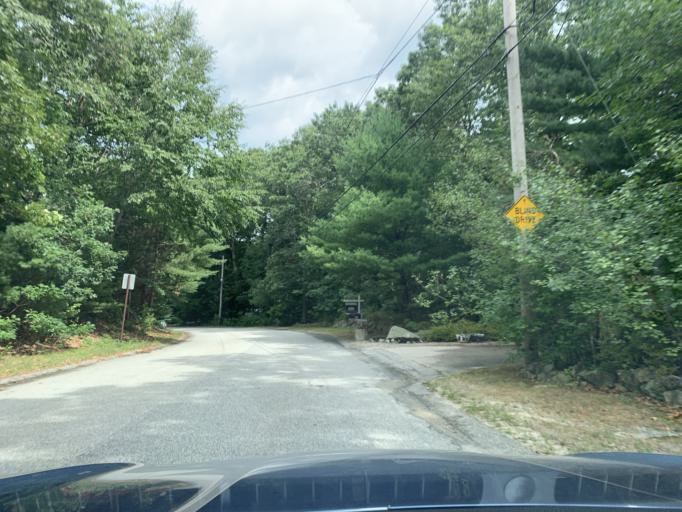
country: US
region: Rhode Island
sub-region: Kent County
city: West Warwick
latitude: 41.7414
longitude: -71.5945
